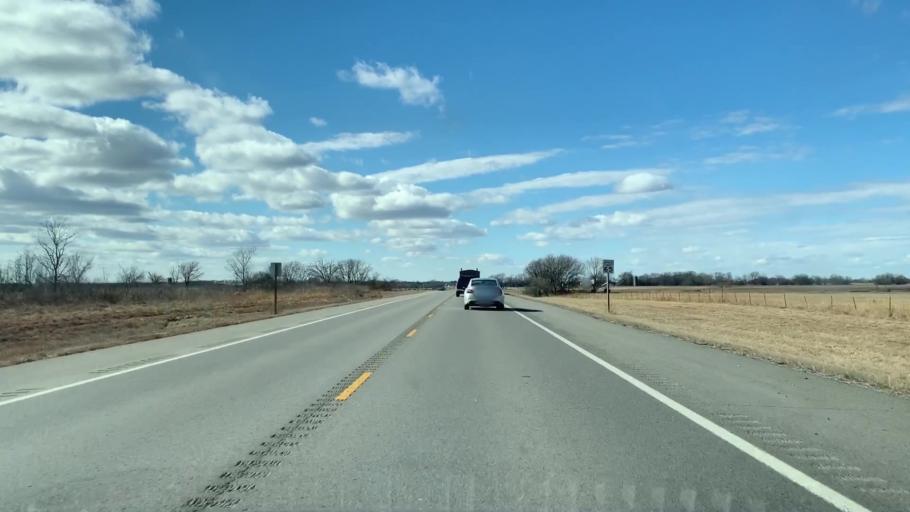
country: US
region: Kansas
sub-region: Crawford County
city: Pittsburg
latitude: 37.3396
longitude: -94.8472
